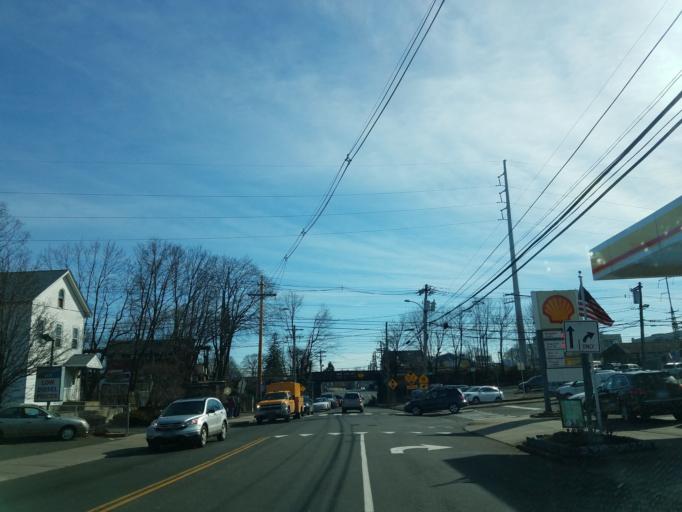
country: US
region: Connecticut
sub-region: Fairfield County
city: East Norwalk
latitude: 41.1048
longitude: -73.4047
